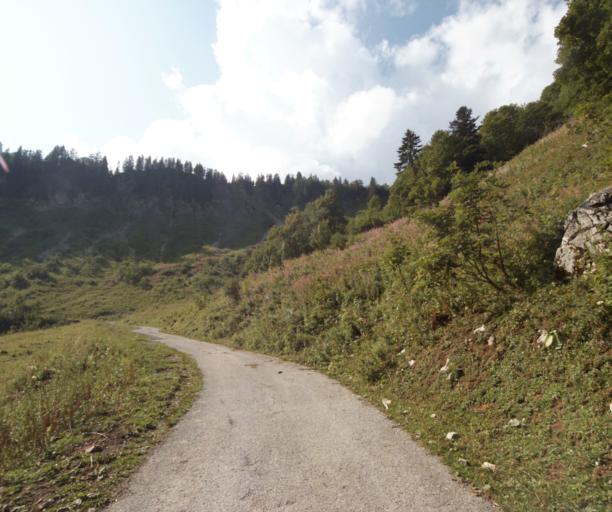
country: CH
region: Vaud
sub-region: Riviera-Pays-d'Enhaut District
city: Caux
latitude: 46.4269
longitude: 6.9980
